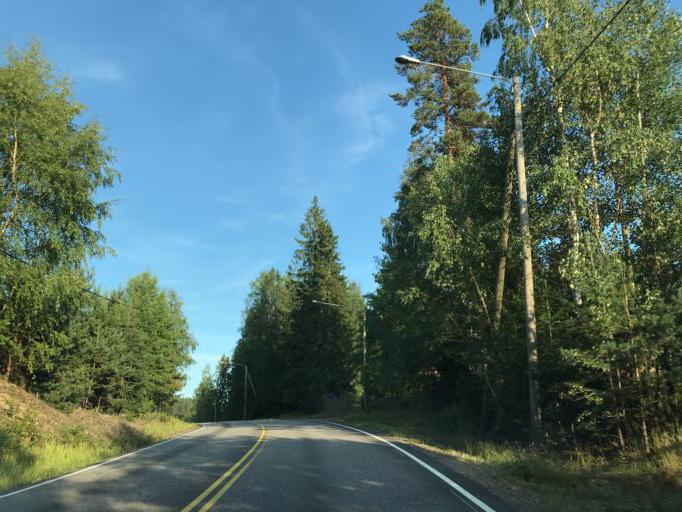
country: FI
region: Uusimaa
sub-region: Helsinki
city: Vihti
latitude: 60.4108
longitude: 24.4415
